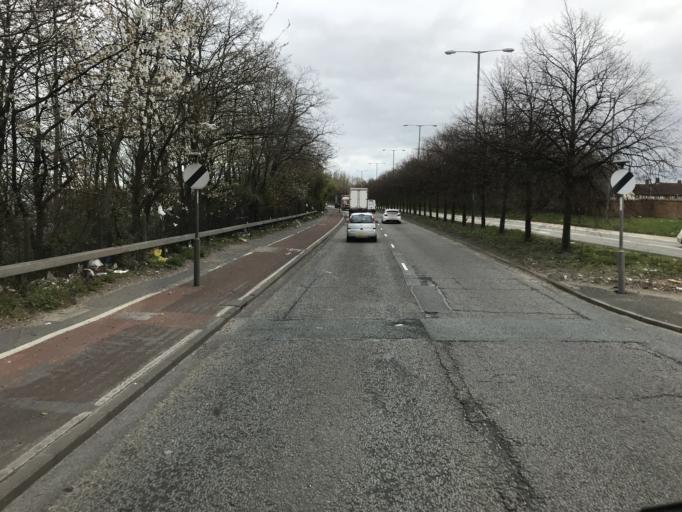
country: GB
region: England
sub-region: Borough of Halton
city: Hale
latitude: 53.3469
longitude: -2.8377
